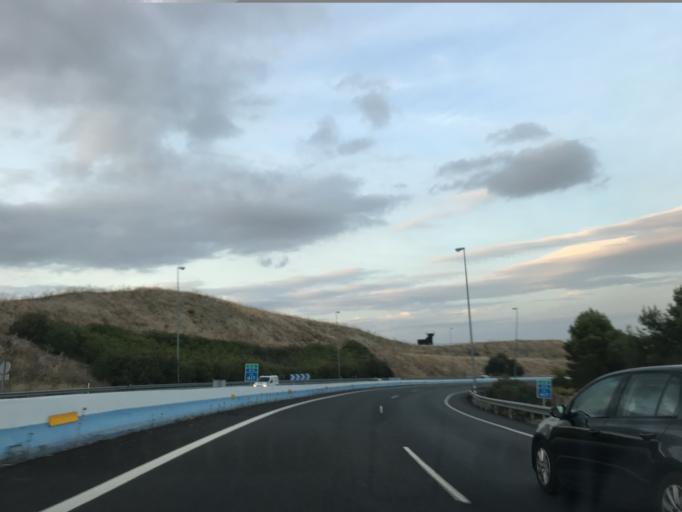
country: ES
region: Andalusia
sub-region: Province of Cordoba
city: La Victoria
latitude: 37.7649
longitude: -4.8225
